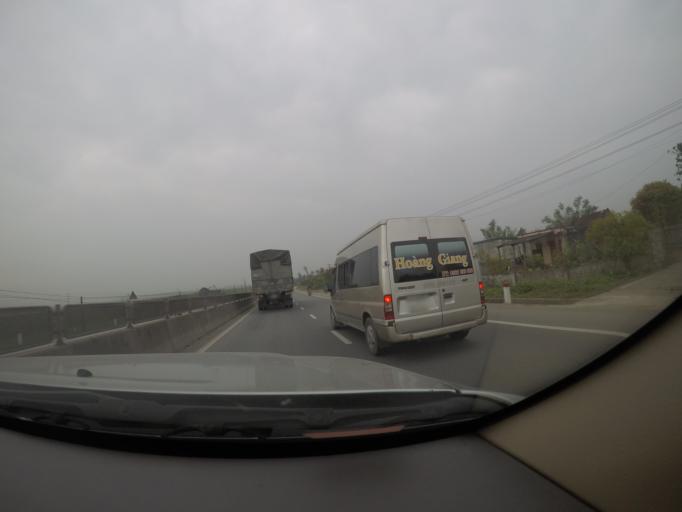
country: VN
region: Ha Tinh
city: Ky Anh
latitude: 18.1554
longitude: 106.2435
